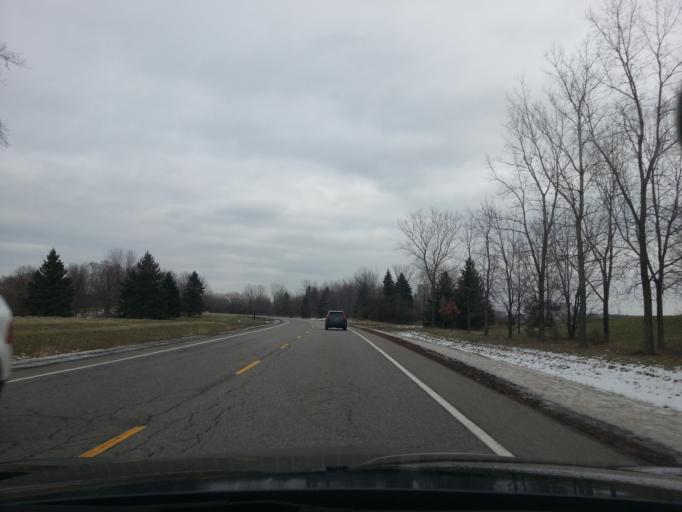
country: CA
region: Quebec
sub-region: Outaouais
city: Gatineau
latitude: 45.4645
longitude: -75.5944
